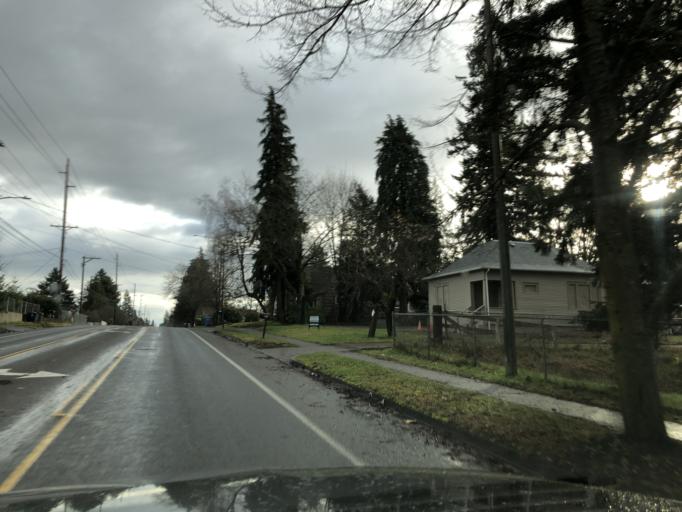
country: US
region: Washington
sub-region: Pierce County
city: Parkland
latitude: 47.1701
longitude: -122.4395
